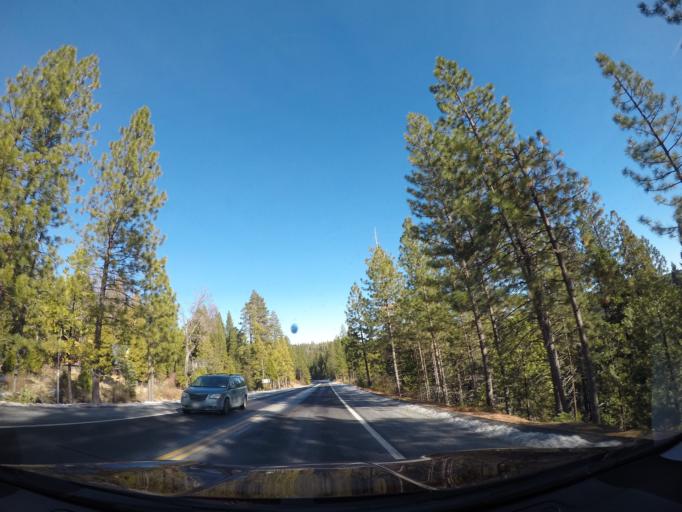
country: US
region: California
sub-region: Tuolumne County
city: Twain Harte
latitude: 38.0856
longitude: -120.1554
